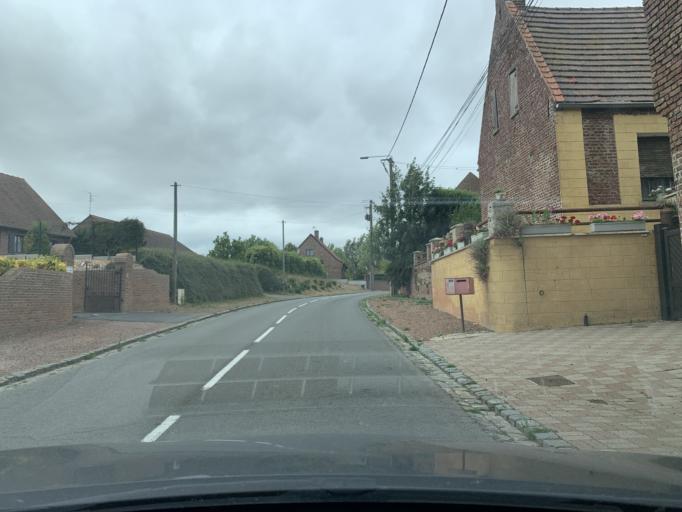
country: FR
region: Nord-Pas-de-Calais
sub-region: Departement du Nord
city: Fechain
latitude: 50.2363
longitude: 3.2100
